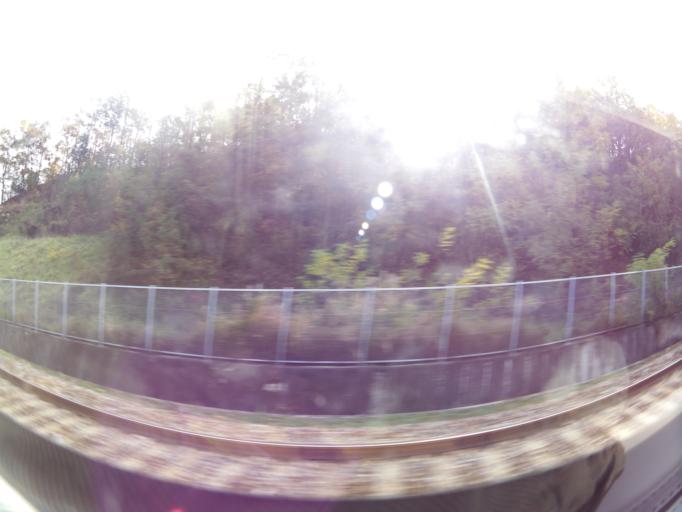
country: KR
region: Daejeon
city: Daejeon
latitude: 36.3356
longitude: 127.4887
